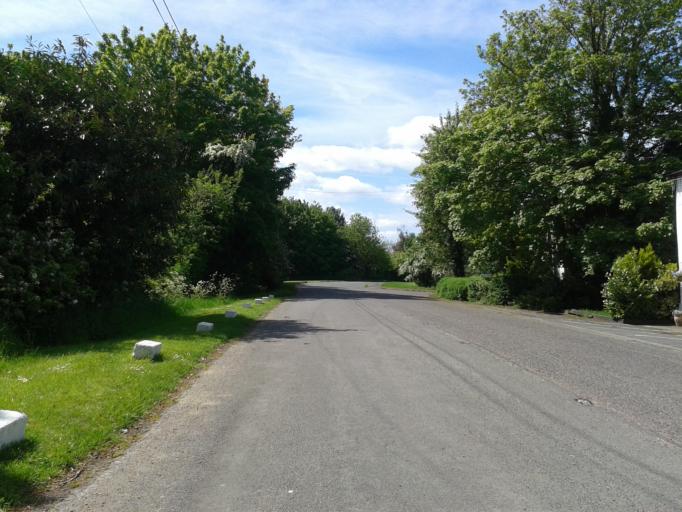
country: GB
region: England
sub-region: Cambridgeshire
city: Melbourn
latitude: 52.1005
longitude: 0.0377
